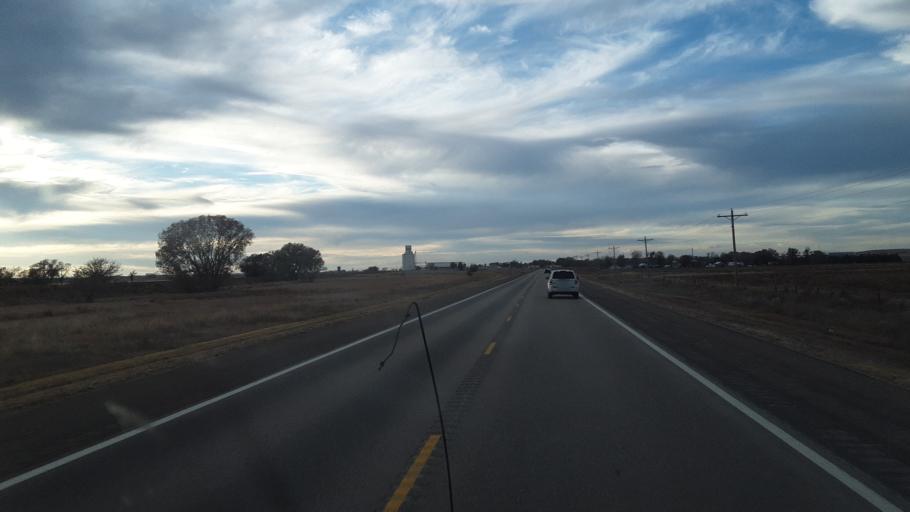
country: US
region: Kansas
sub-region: Hamilton County
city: Syracuse
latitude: 38.0366
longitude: -101.9933
